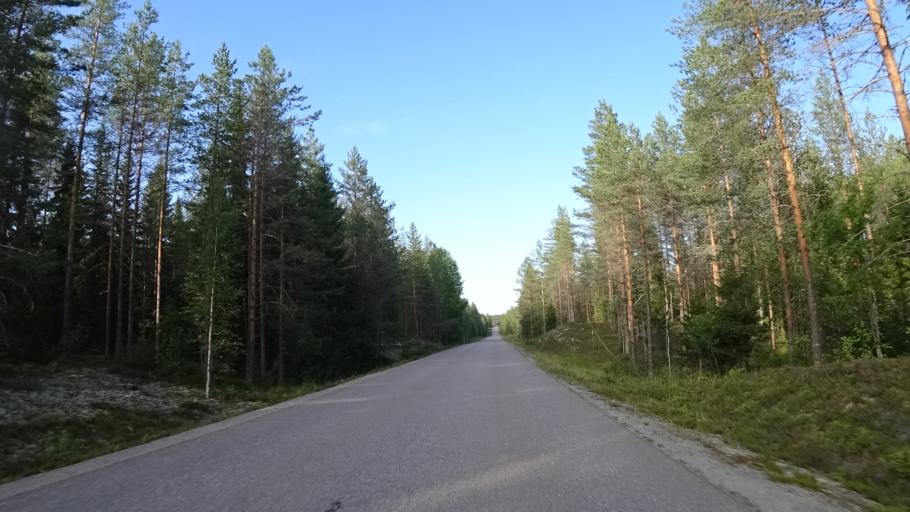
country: FI
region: North Karelia
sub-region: Joensuu
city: Eno
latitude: 63.0605
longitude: 30.5446
